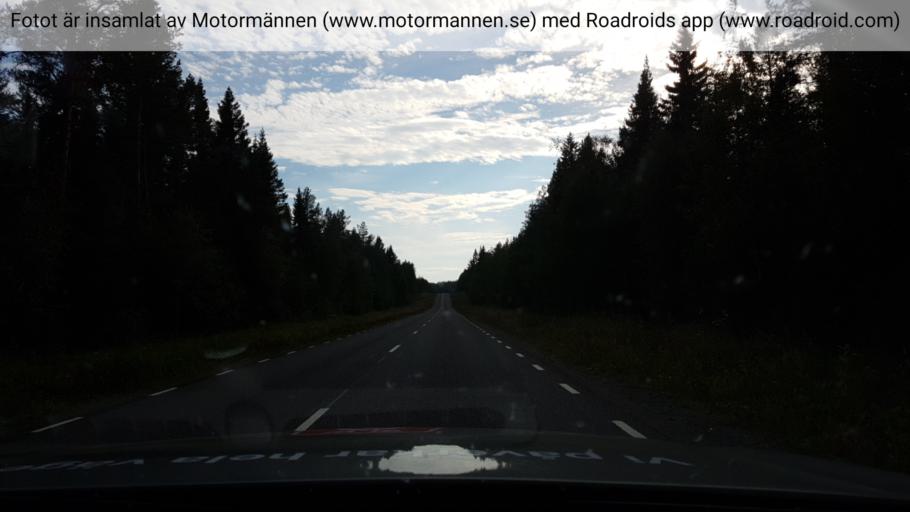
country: SE
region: Vaesternorrland
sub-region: Solleftea Kommun
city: As
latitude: 63.5579
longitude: 16.1408
